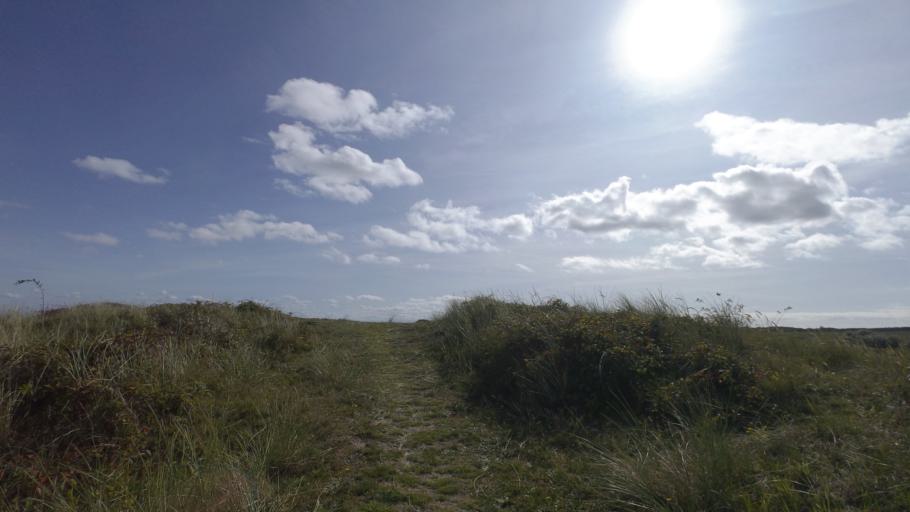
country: NL
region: Friesland
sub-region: Gemeente Ameland
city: Nes
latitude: 53.4528
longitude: 5.7314
